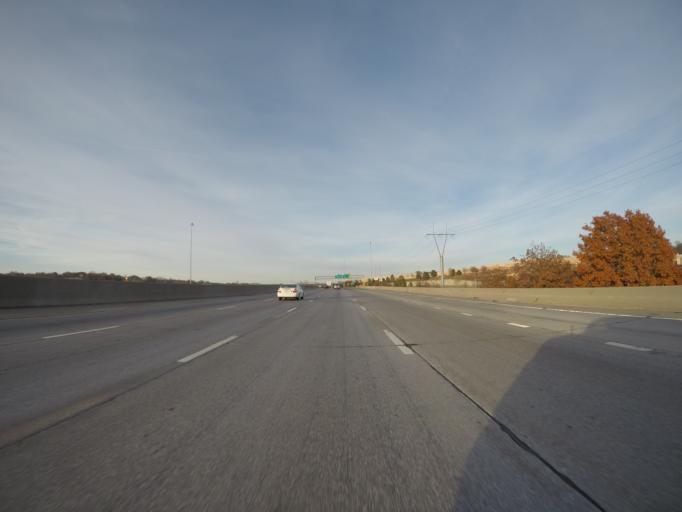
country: US
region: Kansas
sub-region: Johnson County
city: Merriam
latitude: 39.0212
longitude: -94.6923
